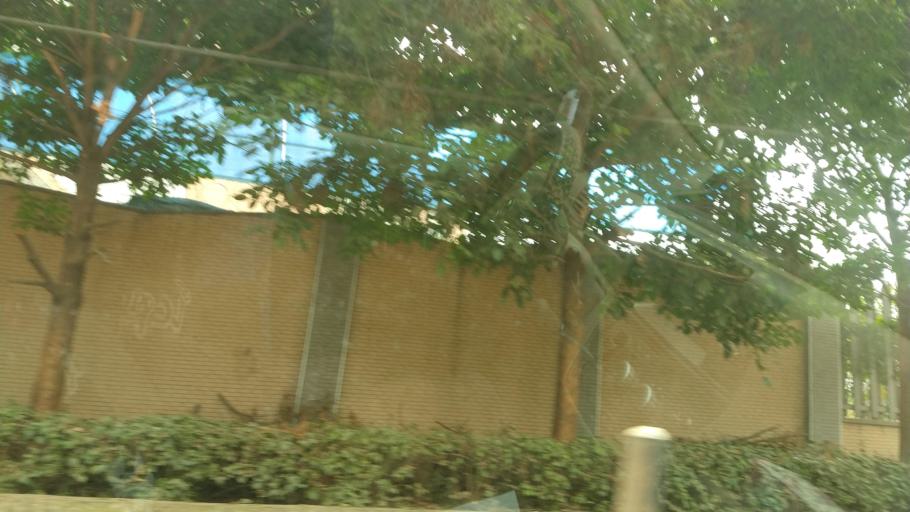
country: KE
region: Nairobi Area
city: Nairobi
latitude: -1.2926
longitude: 36.7764
